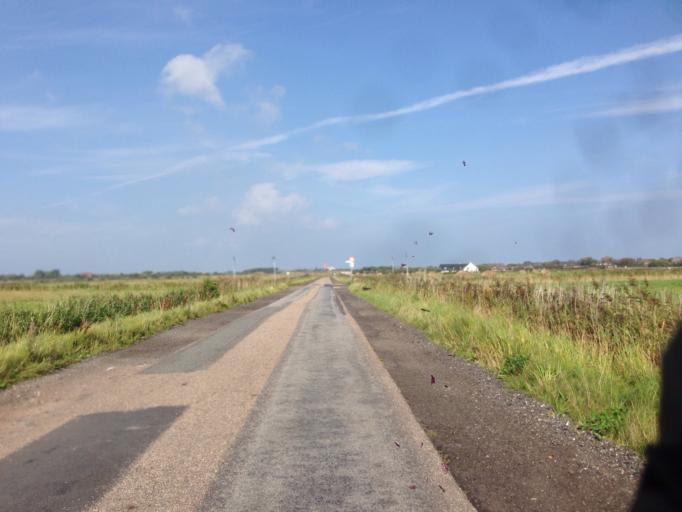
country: DE
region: Schleswig-Holstein
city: Tinnum
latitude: 54.8864
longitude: 8.3509
